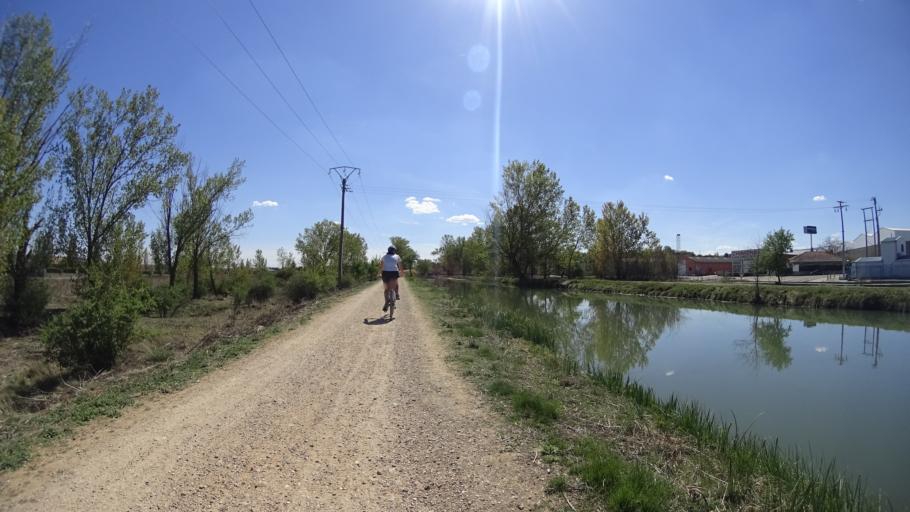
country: ES
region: Castille and Leon
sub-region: Provincia de Valladolid
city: Santovenia de Pisuerga
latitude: 41.6989
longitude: -4.7121
